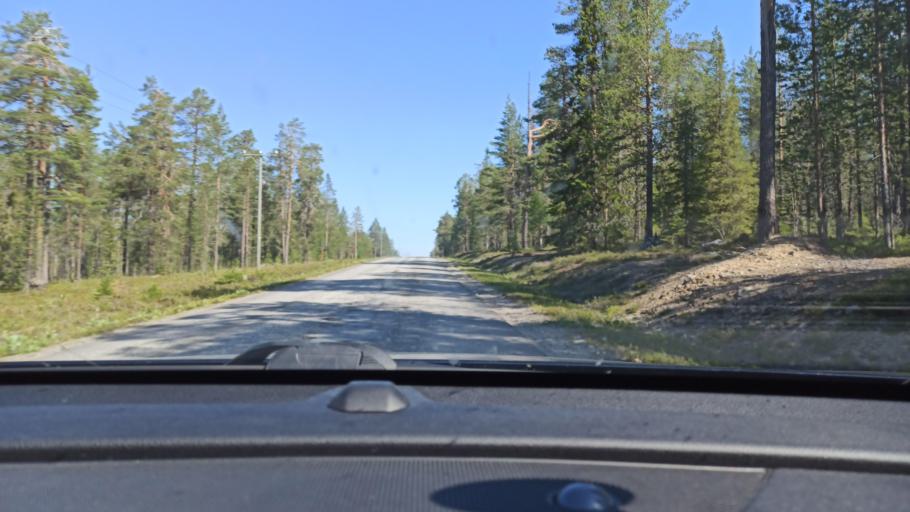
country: FI
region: Lapland
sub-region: Tunturi-Lappi
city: Kolari
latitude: 67.6392
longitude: 24.1571
